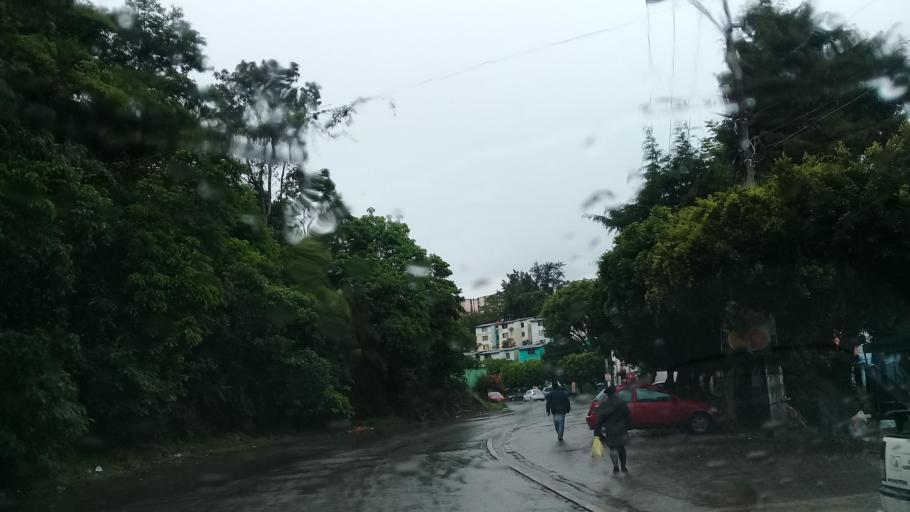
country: MX
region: Veracruz
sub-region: Xalapa
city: Lomas Verdes
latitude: 19.5122
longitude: -96.8998
